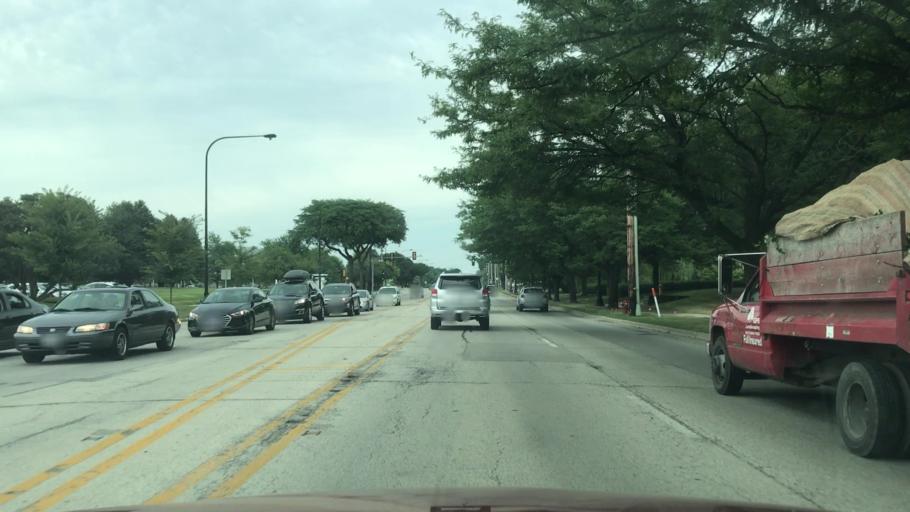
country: US
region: Illinois
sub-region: Cook County
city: Arlington Heights
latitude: 42.0664
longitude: -87.9655
